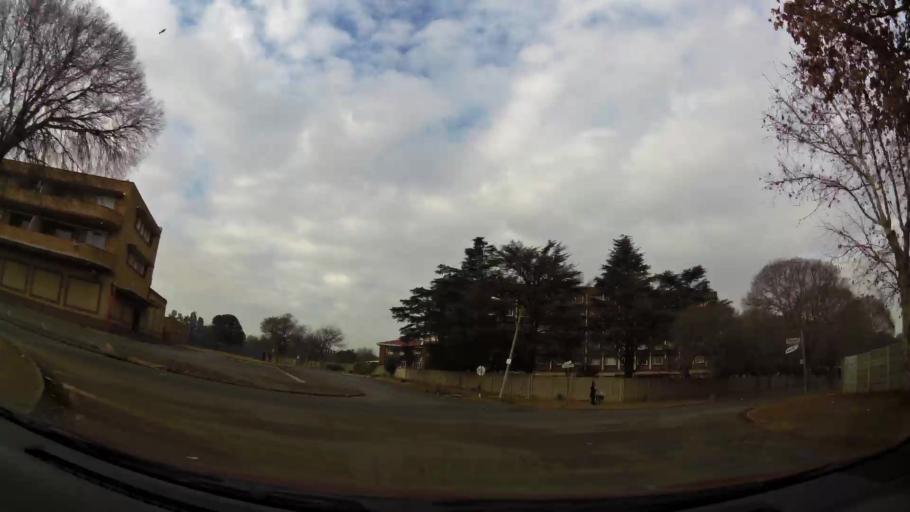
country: ZA
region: Gauteng
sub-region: Sedibeng District Municipality
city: Vanderbijlpark
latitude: -26.6881
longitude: 27.8152
